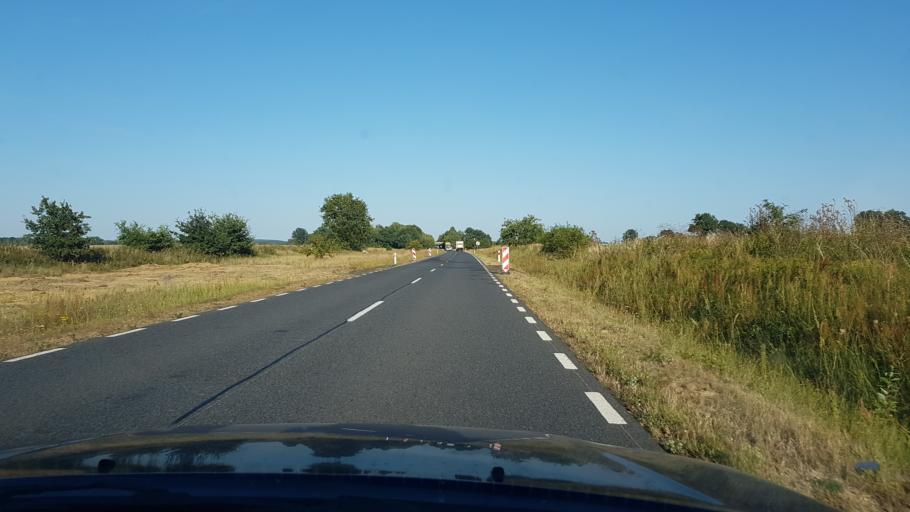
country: PL
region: West Pomeranian Voivodeship
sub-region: Powiat stargardzki
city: Stara Dabrowa
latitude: 53.4330
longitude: 15.1525
